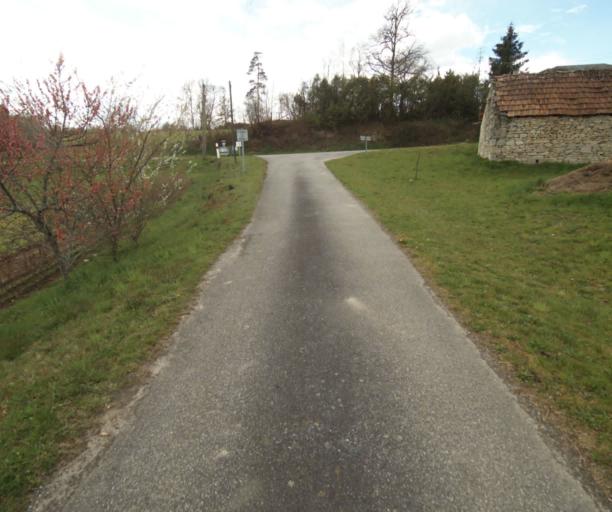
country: FR
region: Limousin
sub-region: Departement de la Correze
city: Argentat
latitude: 45.2118
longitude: 1.9088
